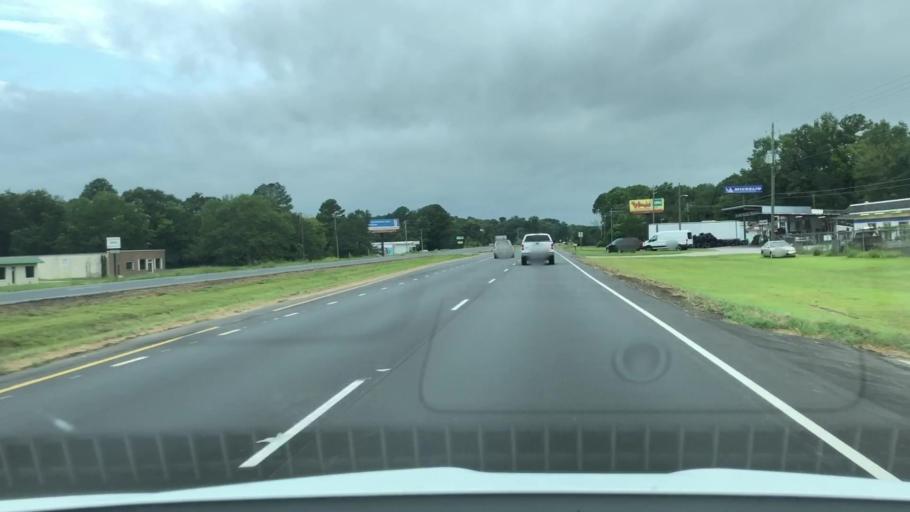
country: US
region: North Carolina
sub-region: Lenoir County
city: Kinston
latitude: 35.2590
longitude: -77.6126
